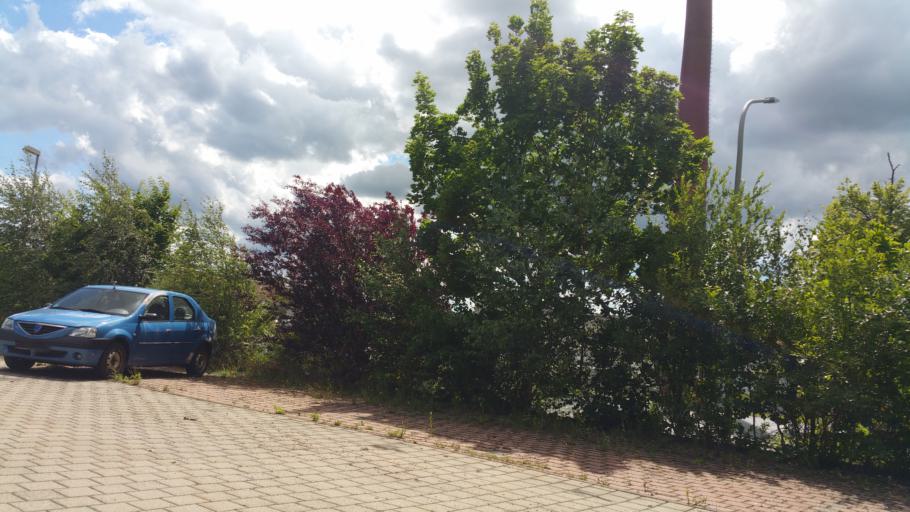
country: DE
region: Bavaria
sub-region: Upper Franconia
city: Schwarzenbach an der Saale
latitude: 50.2182
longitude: 11.9375
